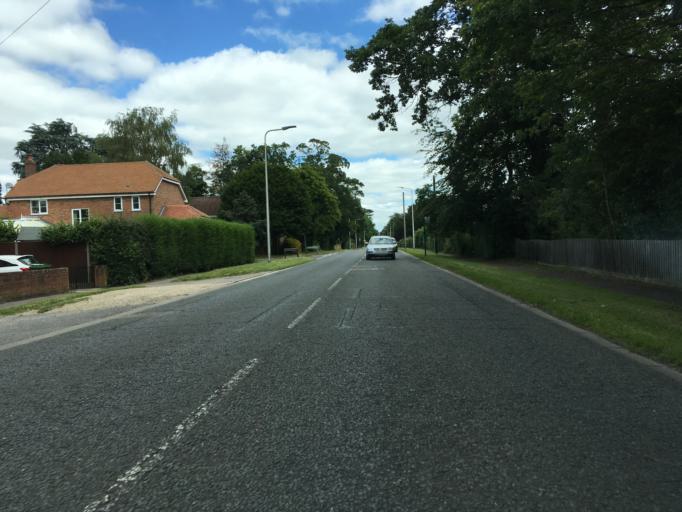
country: GB
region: England
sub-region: West Berkshire
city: Newbury
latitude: 51.3746
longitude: -1.3453
